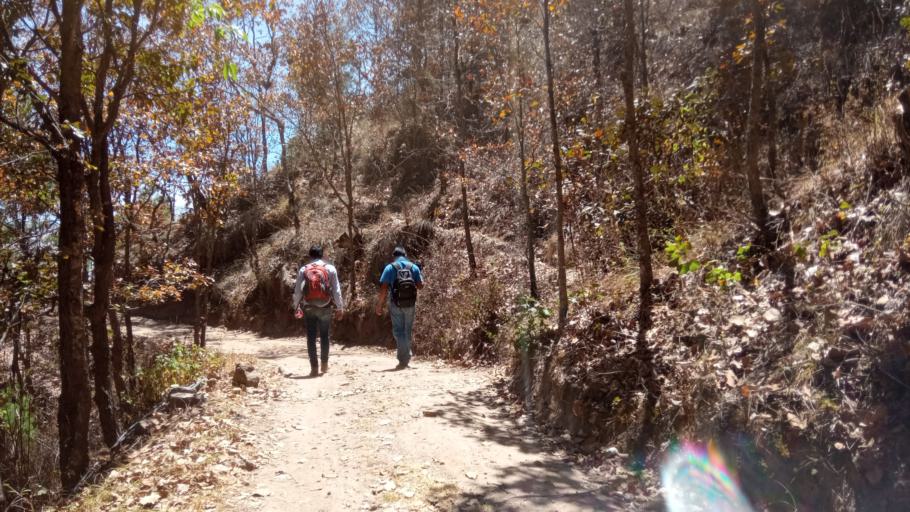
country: GT
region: San Marcos
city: Tejutla
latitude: 15.1323
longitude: -91.7933
